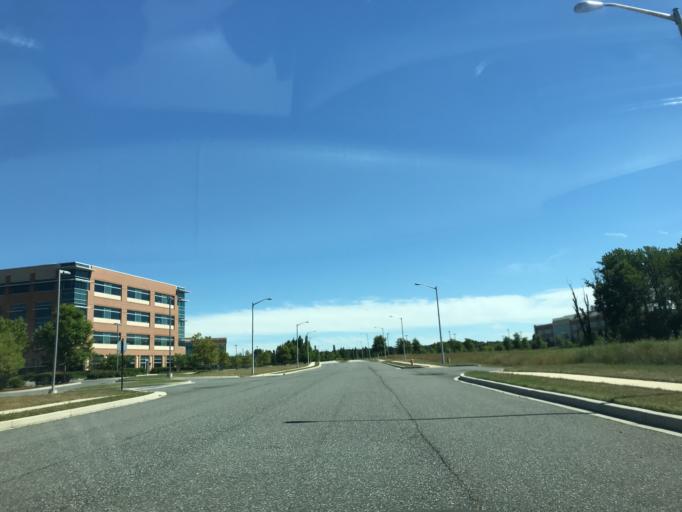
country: US
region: Maryland
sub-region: Harford County
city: Aberdeen
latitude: 39.5053
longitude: -76.1490
